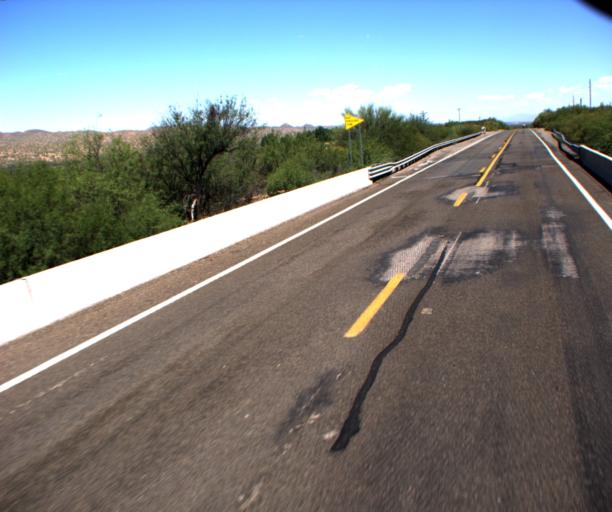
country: US
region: Arizona
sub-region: Pinal County
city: Mammoth
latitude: 32.7871
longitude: -110.6702
